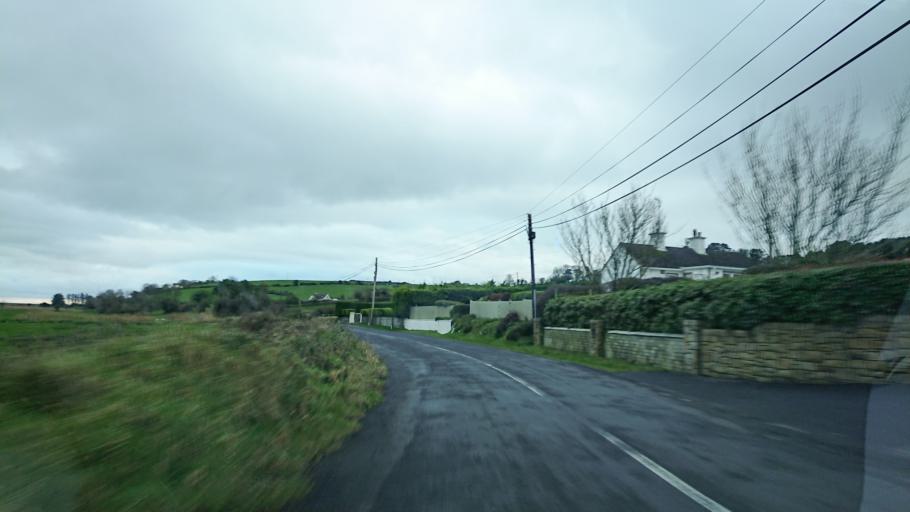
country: IE
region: Munster
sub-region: Waterford
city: Portlaw
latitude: 52.1490
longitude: -7.3795
